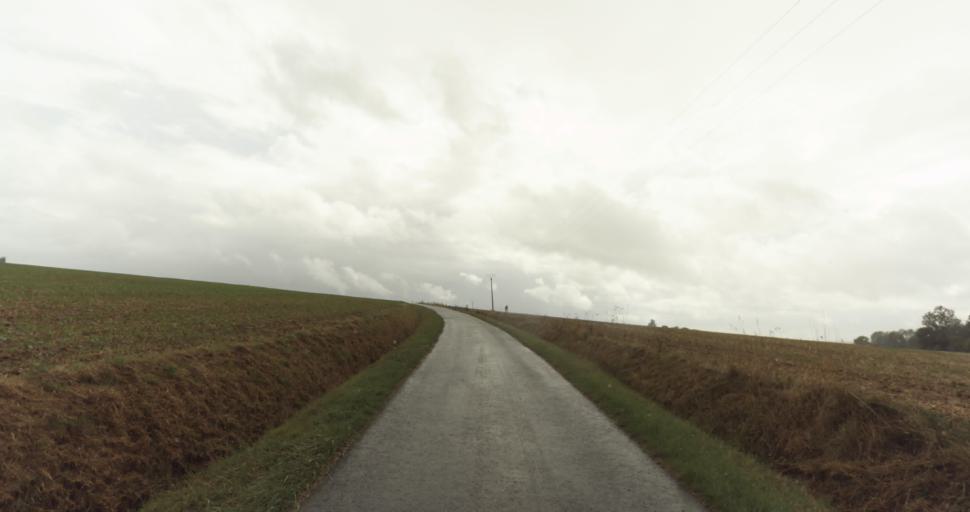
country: FR
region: Lower Normandy
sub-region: Departement de l'Orne
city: Sainte-Gauburge-Sainte-Colombe
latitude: 48.6983
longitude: 0.4068
